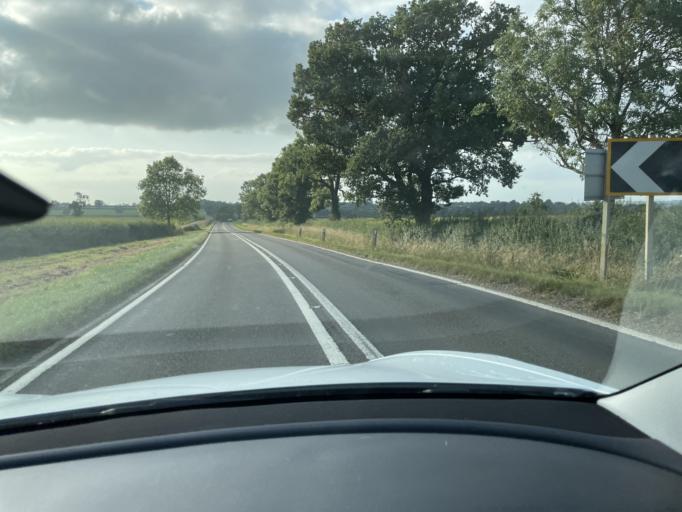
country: GB
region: England
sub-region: Northamptonshire
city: Long Buckby
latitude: 52.4051
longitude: -1.0451
